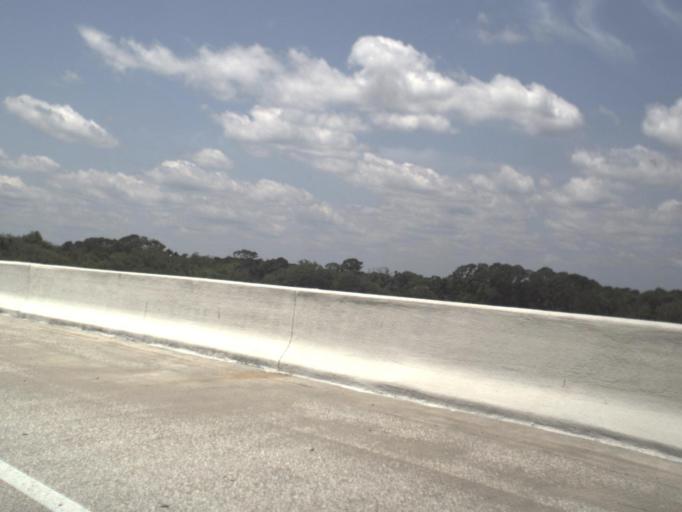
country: US
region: Florida
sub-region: Duval County
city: Jacksonville
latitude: 30.4003
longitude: -81.6660
